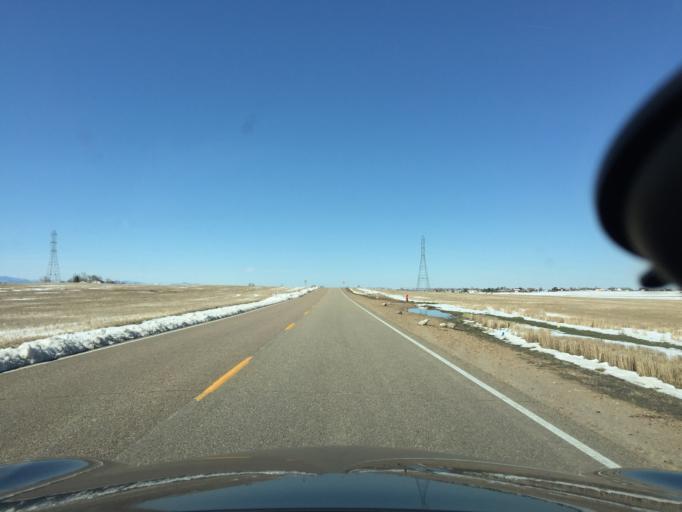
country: US
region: Colorado
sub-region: Boulder County
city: Erie
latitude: 40.0543
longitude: -105.0371
